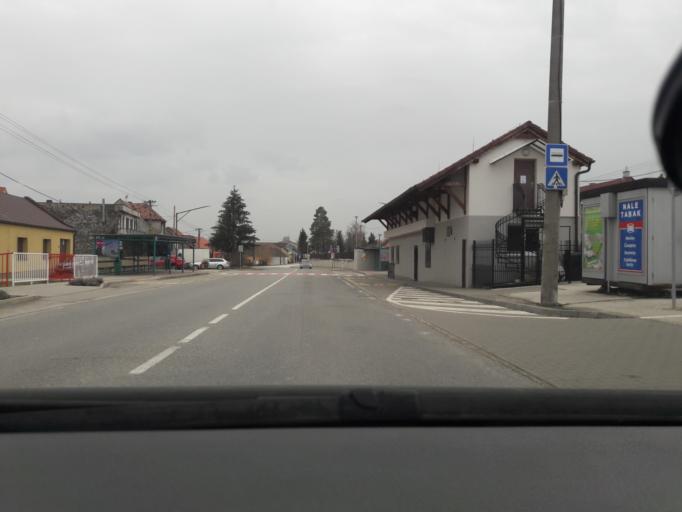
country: SK
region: Bratislavsky
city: Modra
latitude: 48.3559
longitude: 17.4100
